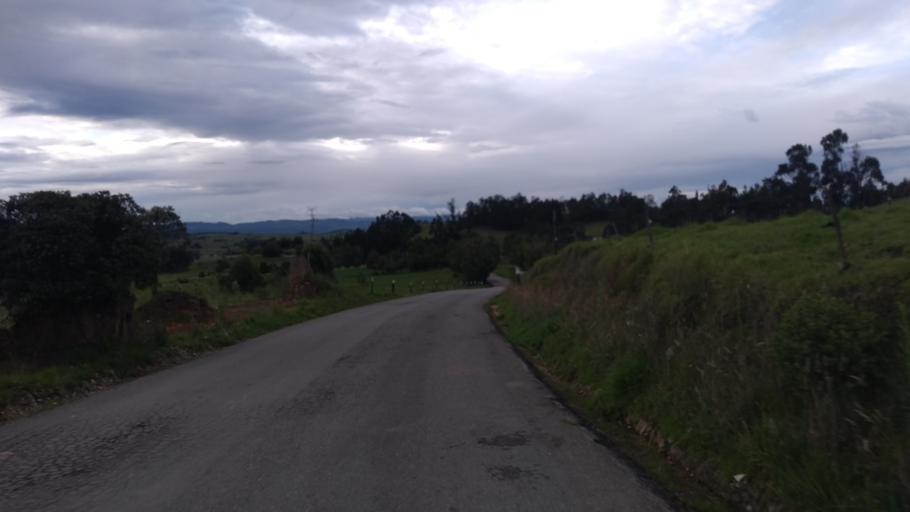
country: CO
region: Boyaca
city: Toca
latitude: 5.5914
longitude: -73.1810
